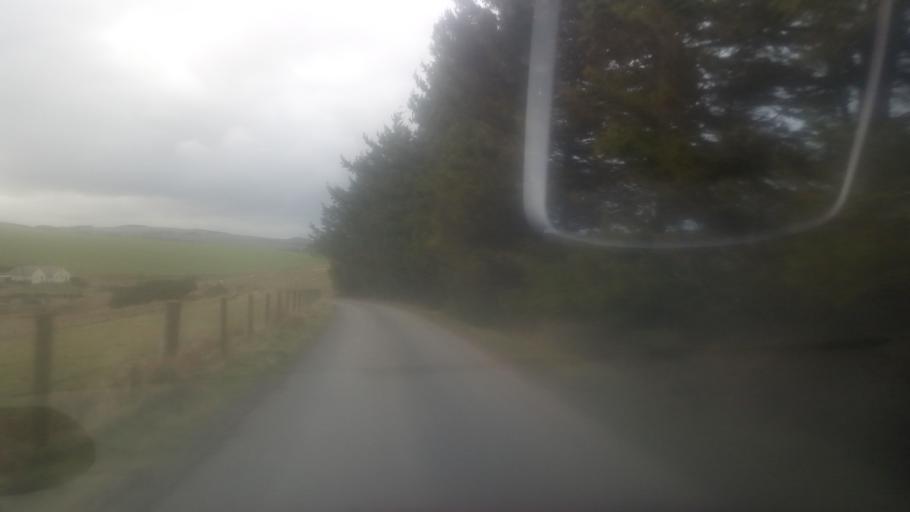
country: GB
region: Scotland
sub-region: The Scottish Borders
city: Jedburgh
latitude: 55.4207
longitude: -2.4927
